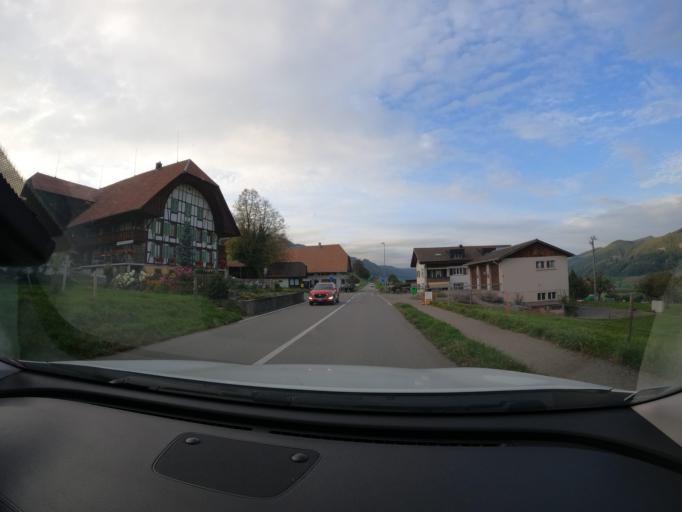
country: CH
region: Bern
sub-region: Bern-Mittelland District
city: Muhlethurnen
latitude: 46.8305
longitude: 7.4985
